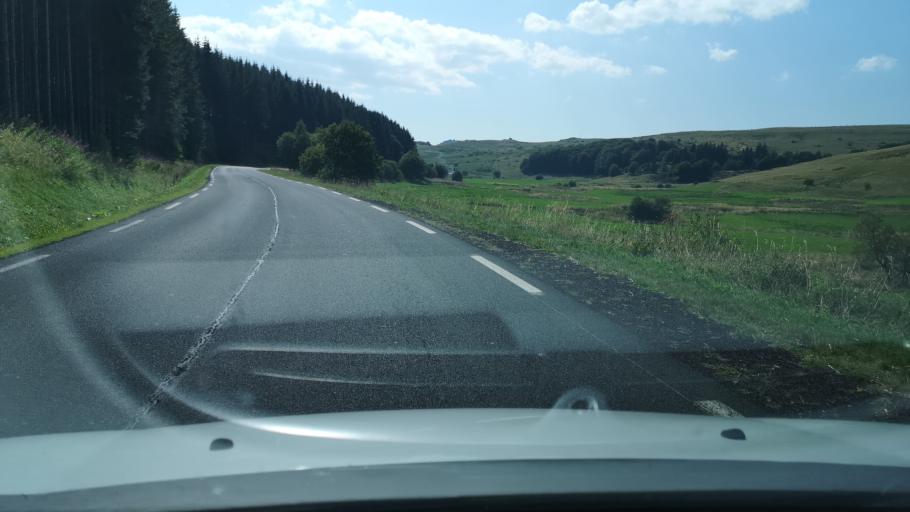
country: FR
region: Auvergne
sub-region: Departement du Puy-de-Dome
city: Mont-Dore
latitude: 45.4944
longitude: 2.8673
